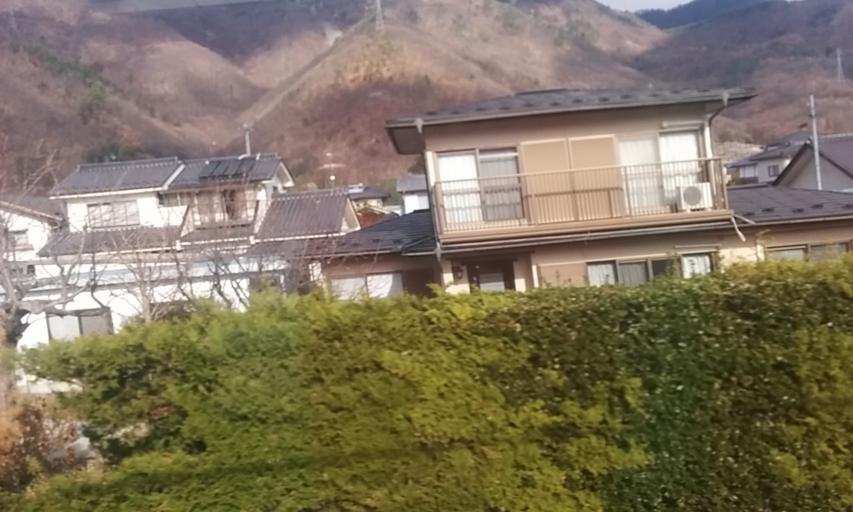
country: JP
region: Nagano
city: Ueda
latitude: 36.4148
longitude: 138.2150
